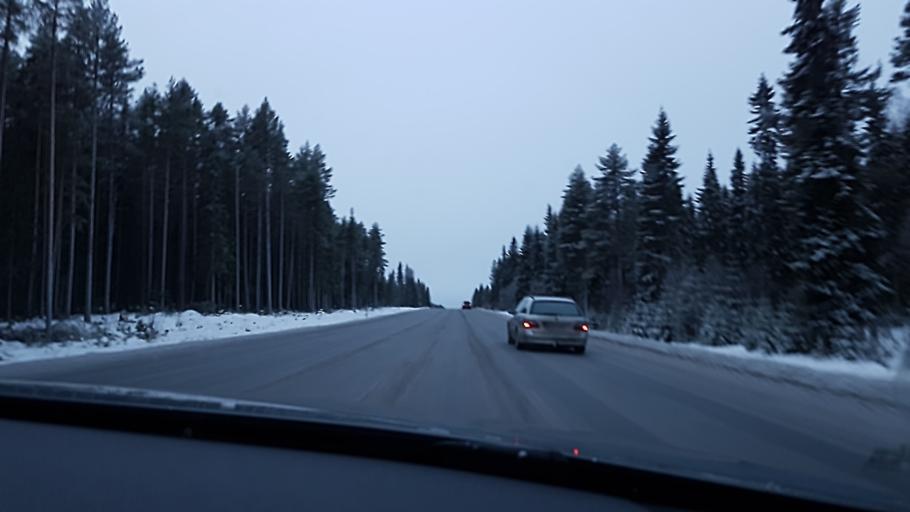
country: SE
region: Jaemtland
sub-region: OEstersunds Kommun
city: Lit
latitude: 63.2525
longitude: 14.8116
